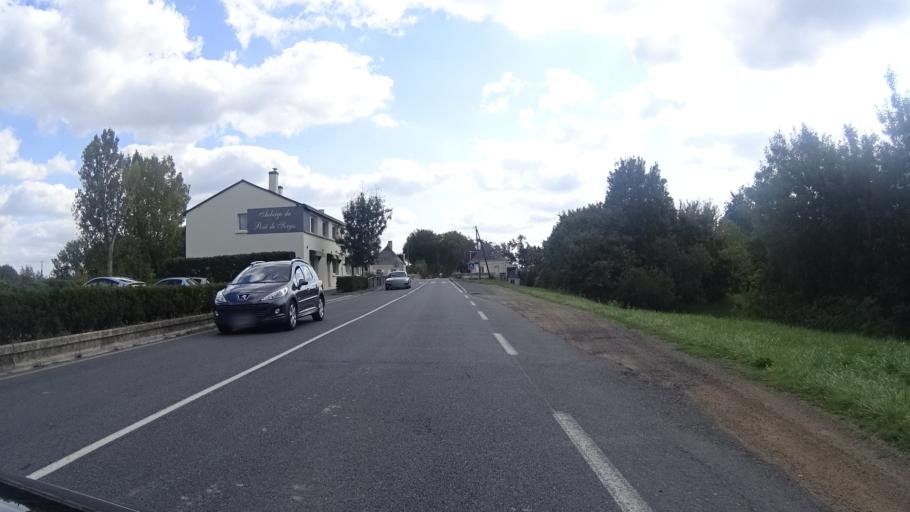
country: FR
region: Pays de la Loire
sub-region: Departement de Maine-et-Loire
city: Trelaze
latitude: 47.4309
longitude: -0.4729
